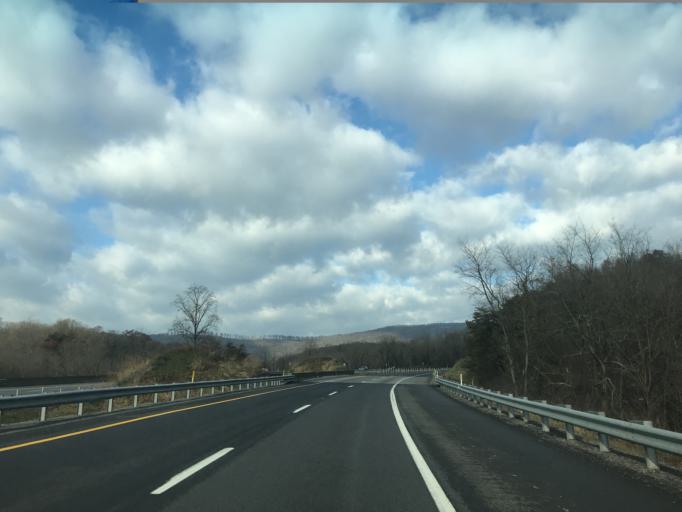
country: US
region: Maryland
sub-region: Washington County
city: Hancock
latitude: 39.8060
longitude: -78.2693
